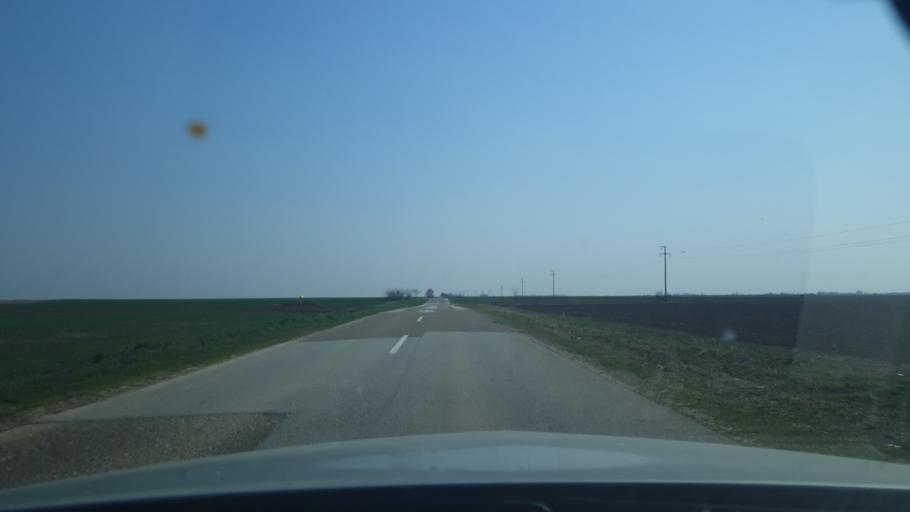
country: RS
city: Sasinci
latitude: 45.0428
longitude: 19.7284
